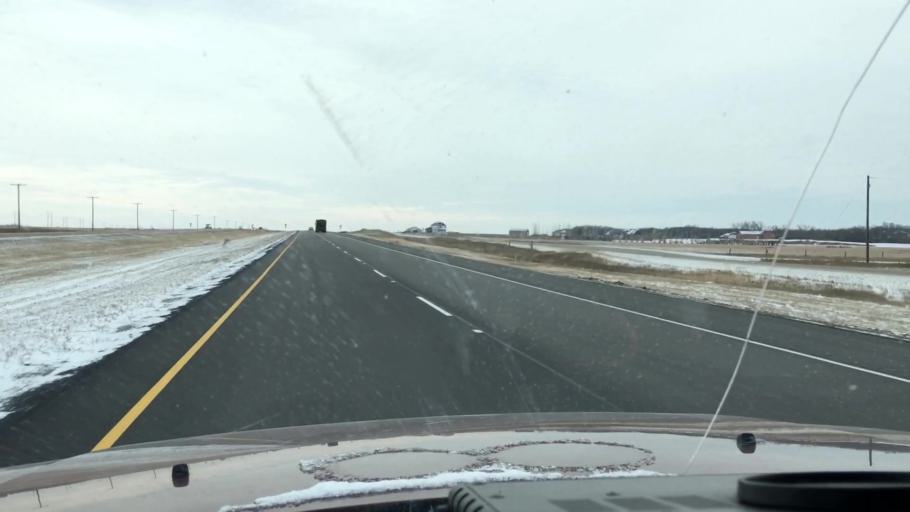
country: CA
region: Saskatchewan
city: Saskatoon
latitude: 51.9337
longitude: -106.5370
